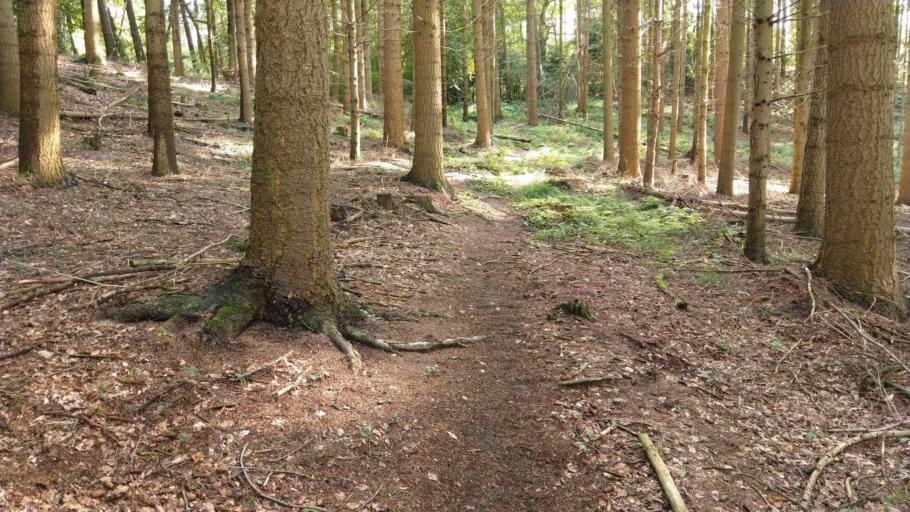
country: DE
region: North Rhine-Westphalia
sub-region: Regierungsbezirk Koln
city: Aachen
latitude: 50.7453
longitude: 6.0705
